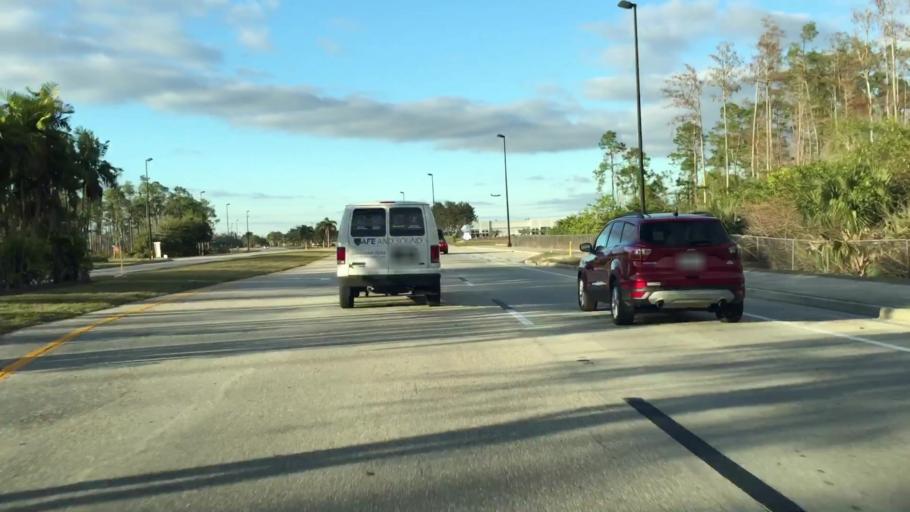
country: US
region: Florida
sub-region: Lee County
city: Three Oaks
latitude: 26.4966
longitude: -81.7841
